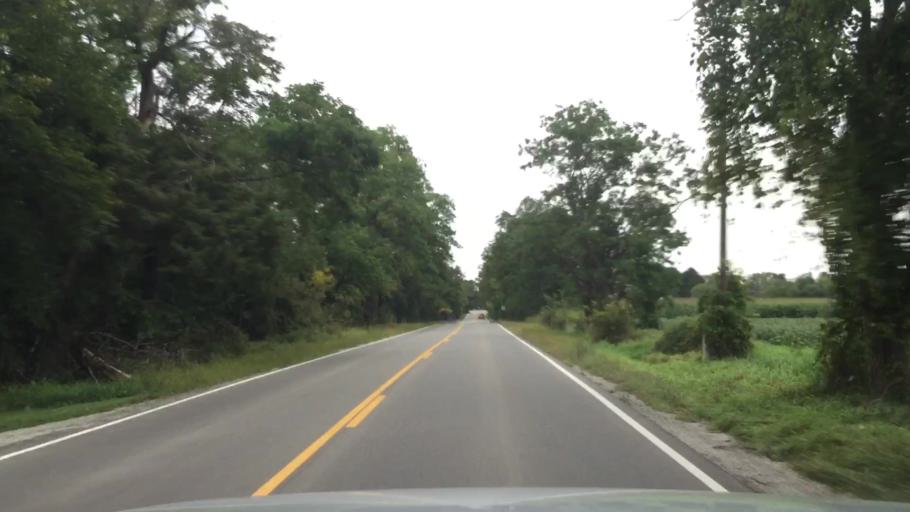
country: US
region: Michigan
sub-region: Washtenaw County
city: Ypsilanti
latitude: 42.1974
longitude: -83.6284
